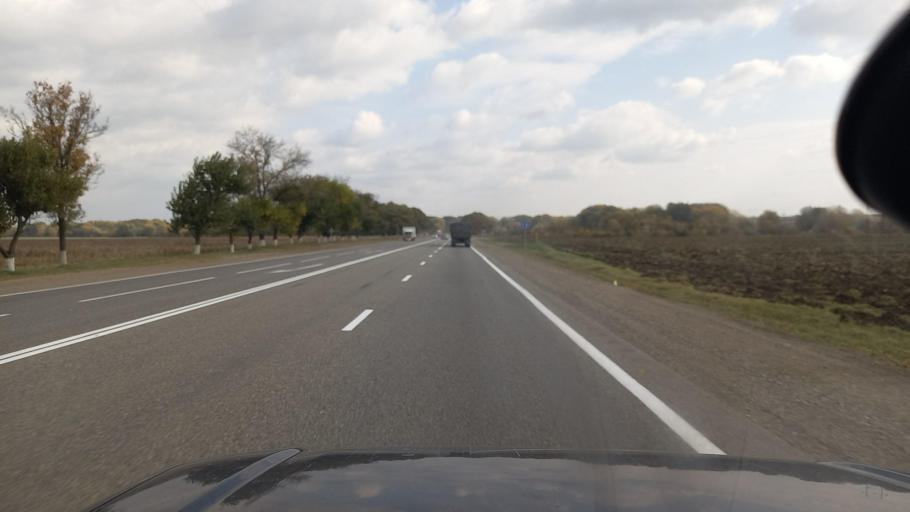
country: RU
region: Krasnodarskiy
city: Kholmskiy
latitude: 44.8511
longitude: 38.4386
